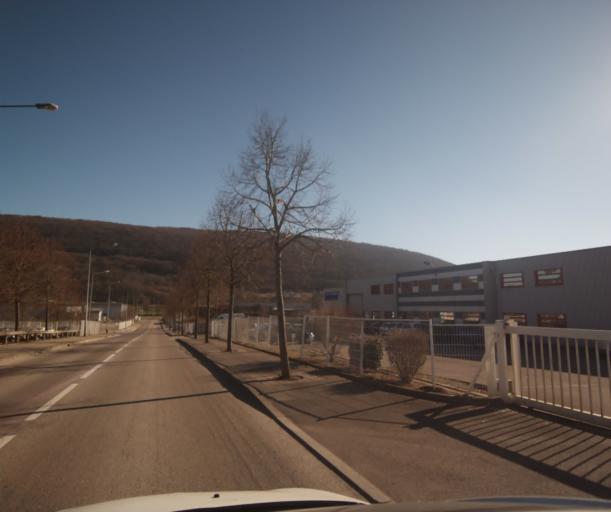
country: FR
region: Franche-Comte
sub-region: Departement du Doubs
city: Avanne-Aveney
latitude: 47.2133
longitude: 5.9698
